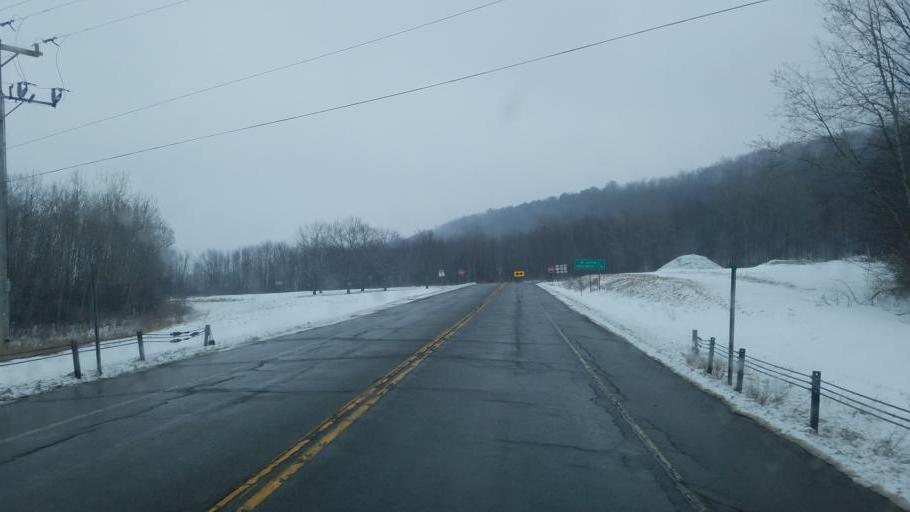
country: US
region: New York
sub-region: Steuben County
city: Canisteo
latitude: 42.1183
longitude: -77.5295
